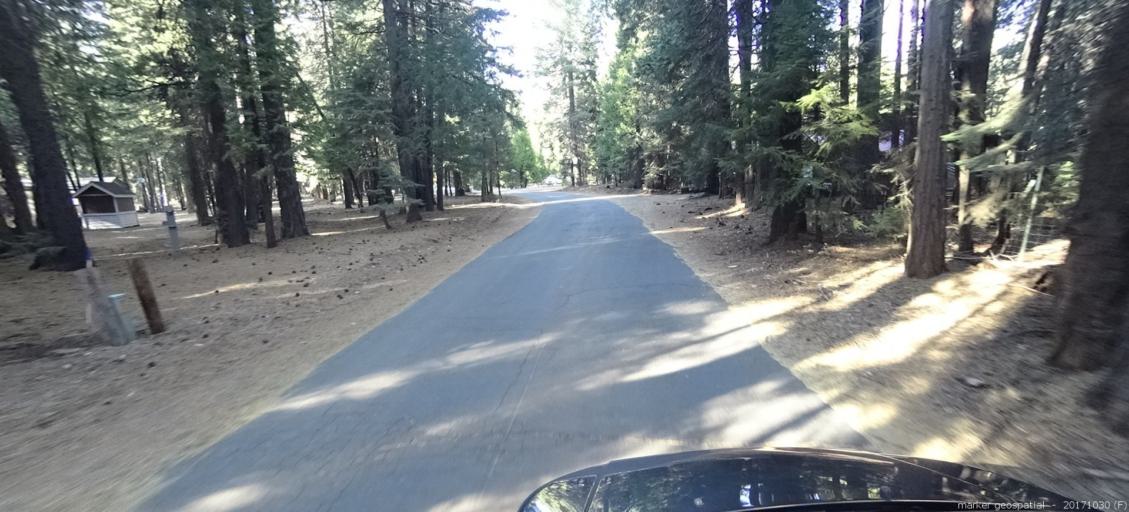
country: US
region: California
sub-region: Shasta County
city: Shingletown
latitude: 40.5570
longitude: -121.7347
